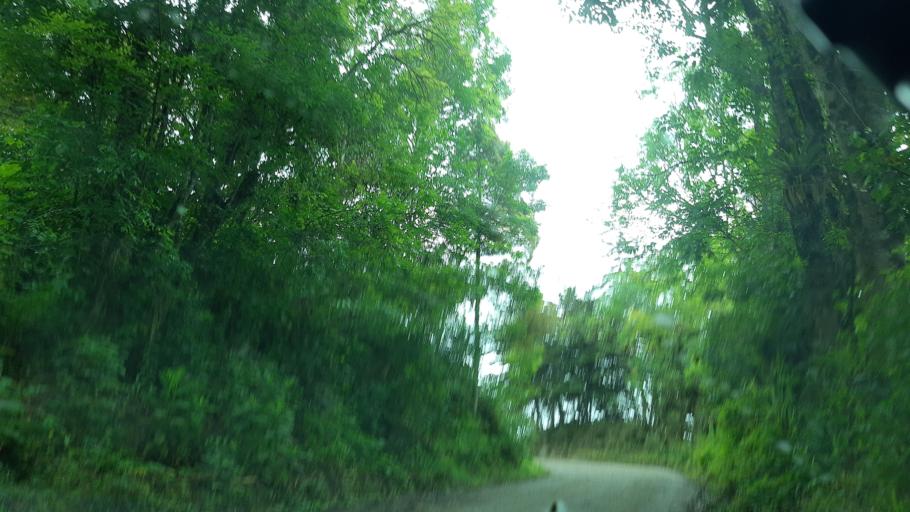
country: CO
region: Boyaca
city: Guateque
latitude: 5.0320
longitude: -73.4472
